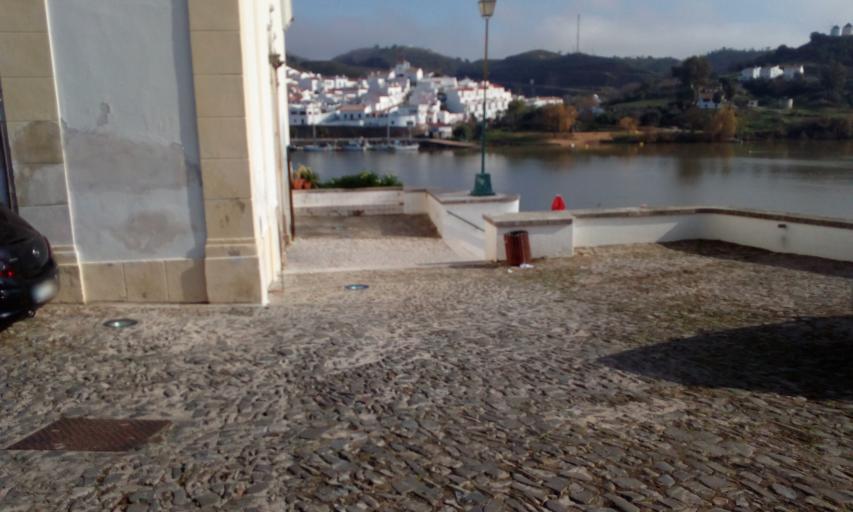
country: PT
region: Faro
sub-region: Alcoutim
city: Alcoutim
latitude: 37.4718
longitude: -7.4714
